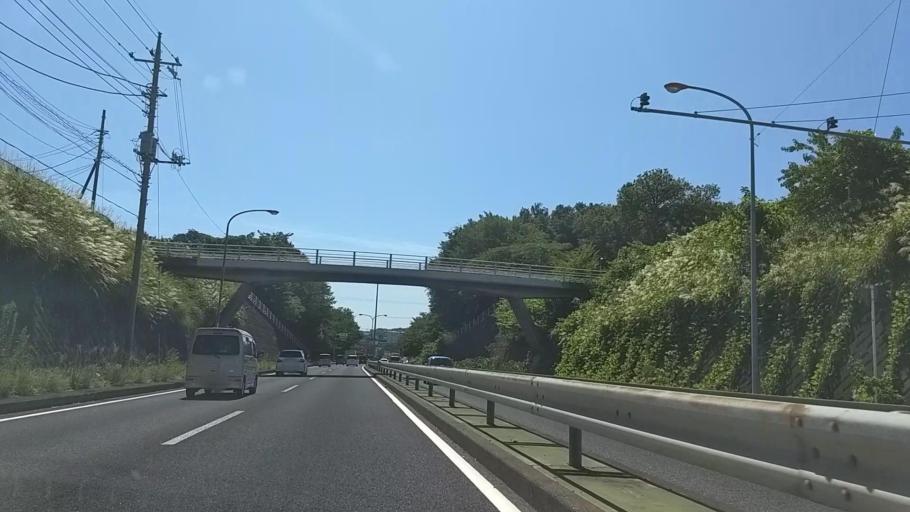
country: JP
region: Kanagawa
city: Zama
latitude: 35.5338
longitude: 139.3621
